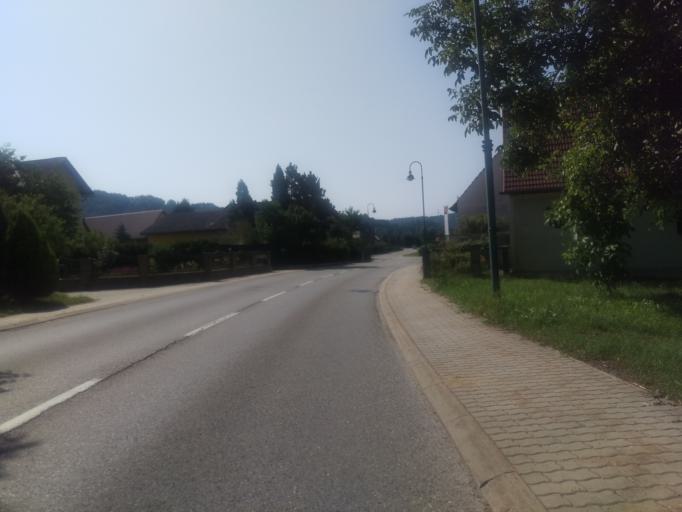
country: AT
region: Styria
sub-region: Politischer Bezirk Graz-Umgebung
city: Fernitz
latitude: 46.9672
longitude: 15.5034
